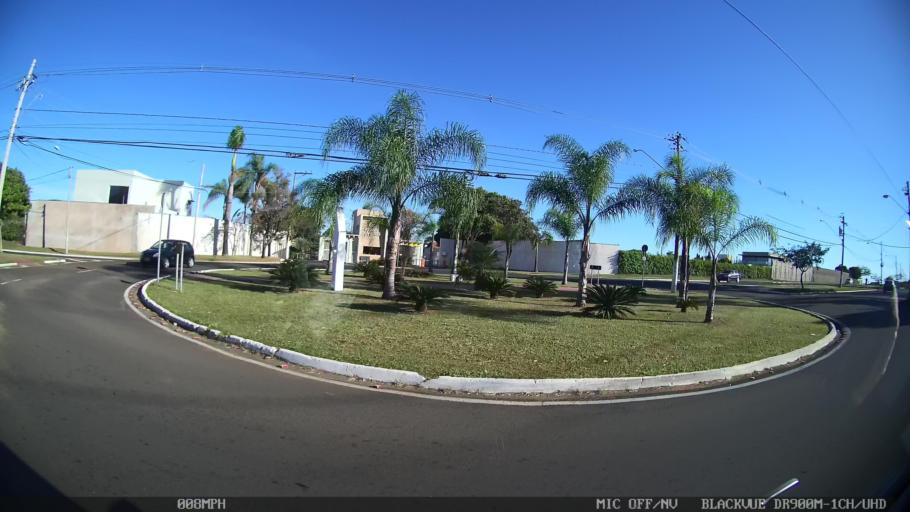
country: BR
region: Sao Paulo
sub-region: Franca
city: Franca
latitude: -20.5659
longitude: -47.3653
